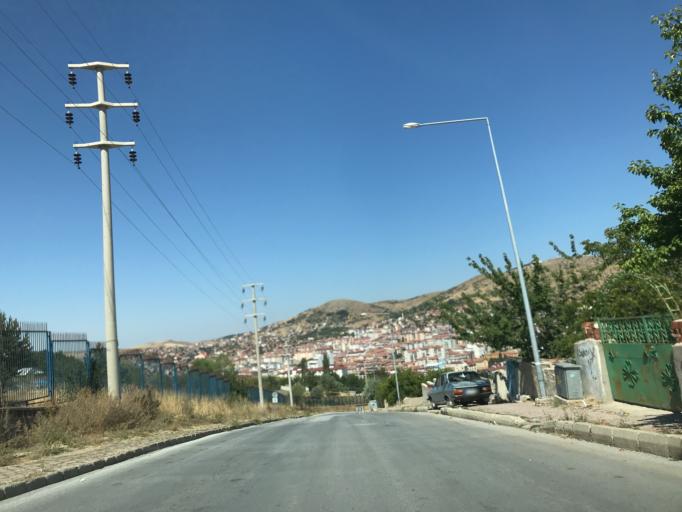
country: TR
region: Yozgat
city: Yozgat
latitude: 39.8162
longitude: 34.8213
